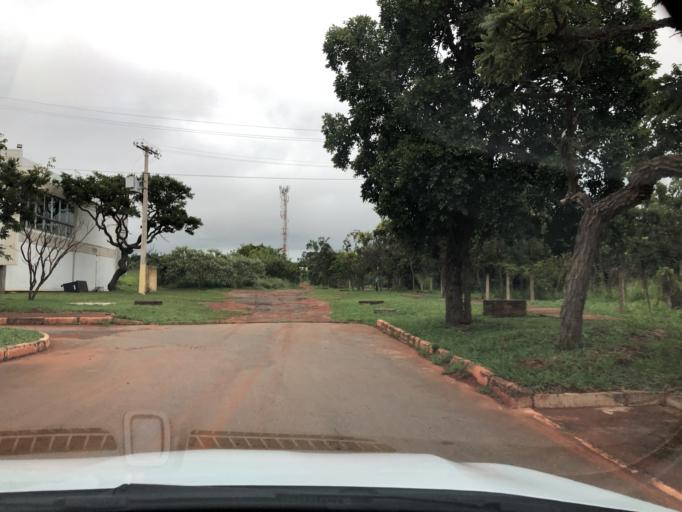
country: BR
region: Federal District
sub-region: Brasilia
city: Brasilia
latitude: -15.7721
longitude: -47.8671
